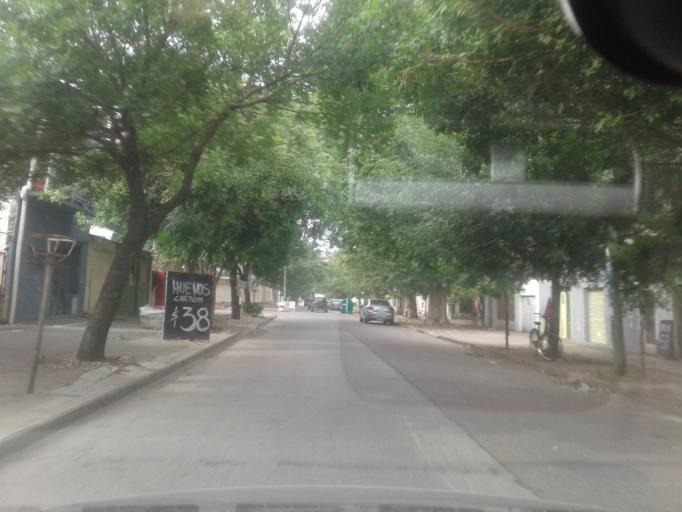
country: AR
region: Santa Fe
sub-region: Departamento de Rosario
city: Rosario
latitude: -32.9708
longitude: -60.6487
